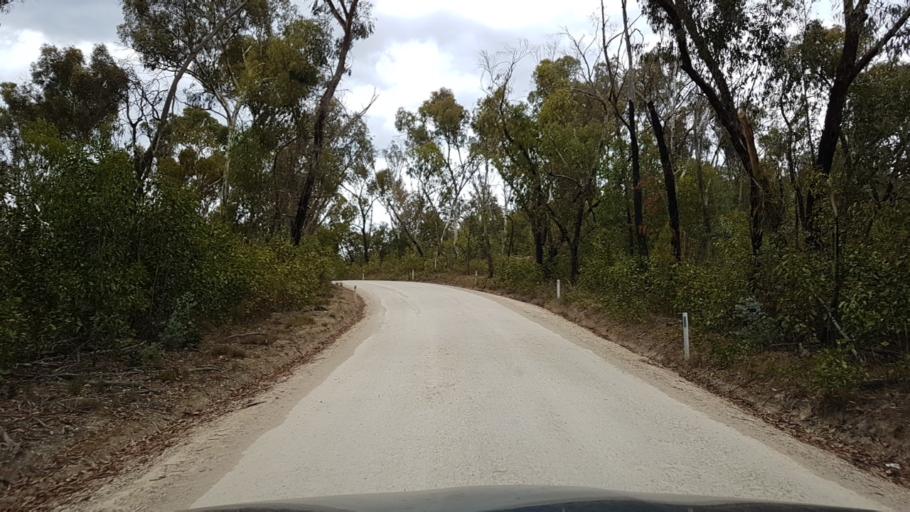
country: AU
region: South Australia
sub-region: Adelaide Hills
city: Gumeracha
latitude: -34.7934
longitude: 138.8345
